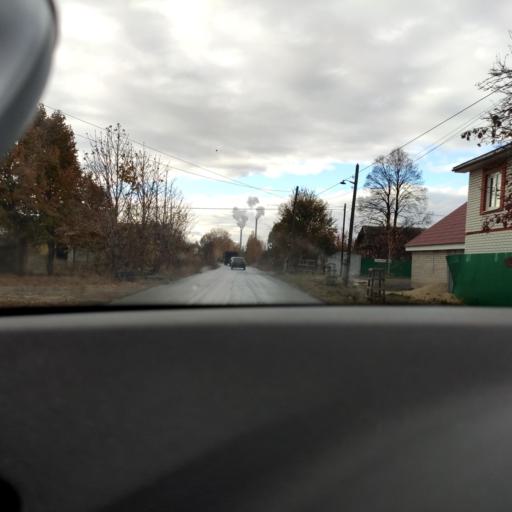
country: RU
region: Samara
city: Petra-Dubrava
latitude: 53.2485
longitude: 50.3241
